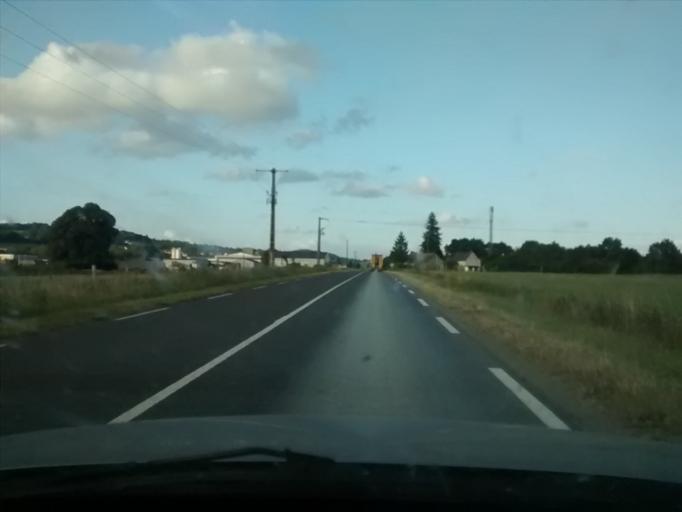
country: FR
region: Pays de la Loire
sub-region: Departement de la Sarthe
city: Sille-le-Guillaume
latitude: 48.1718
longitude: -0.1545
